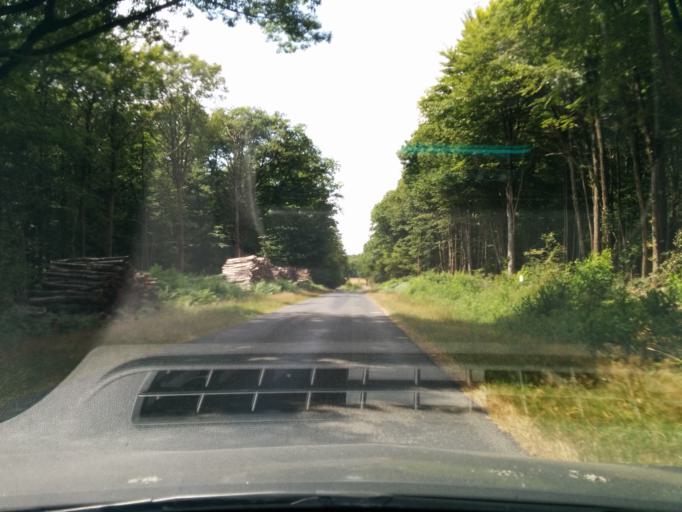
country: FR
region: Centre
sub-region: Departement du Cher
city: Henrichemont
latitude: 47.3494
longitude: 2.6226
